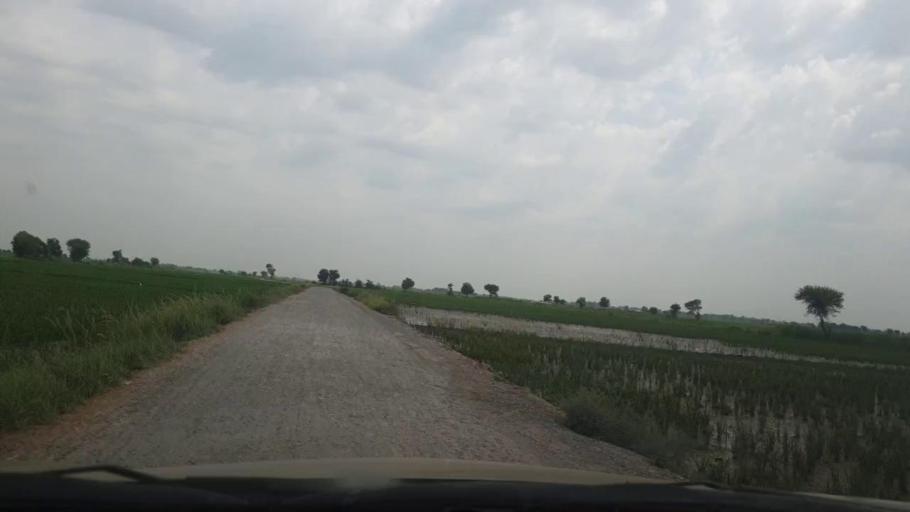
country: PK
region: Sindh
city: Ratodero
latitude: 27.7157
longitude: 68.2281
